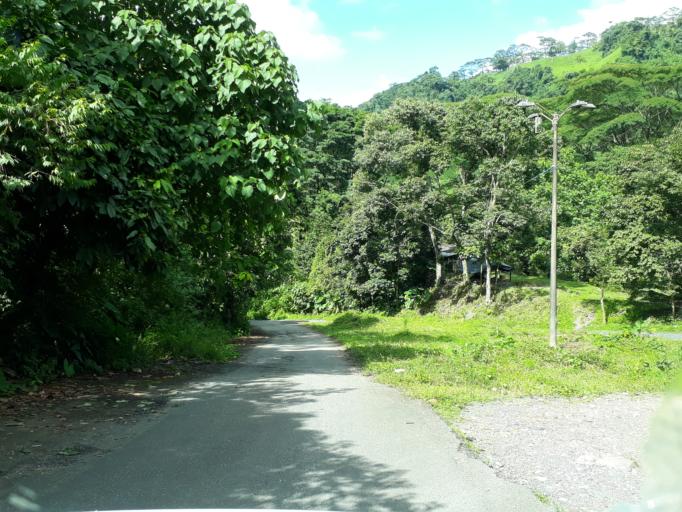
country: CO
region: Boyaca
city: Santa Maria
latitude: 4.7430
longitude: -73.3380
